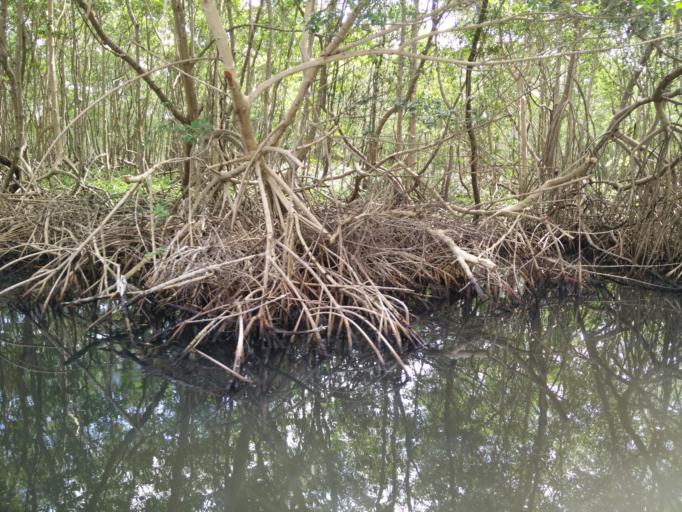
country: GP
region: Guadeloupe
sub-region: Guadeloupe
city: Petit-Canal
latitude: 16.3488
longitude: -61.4872
